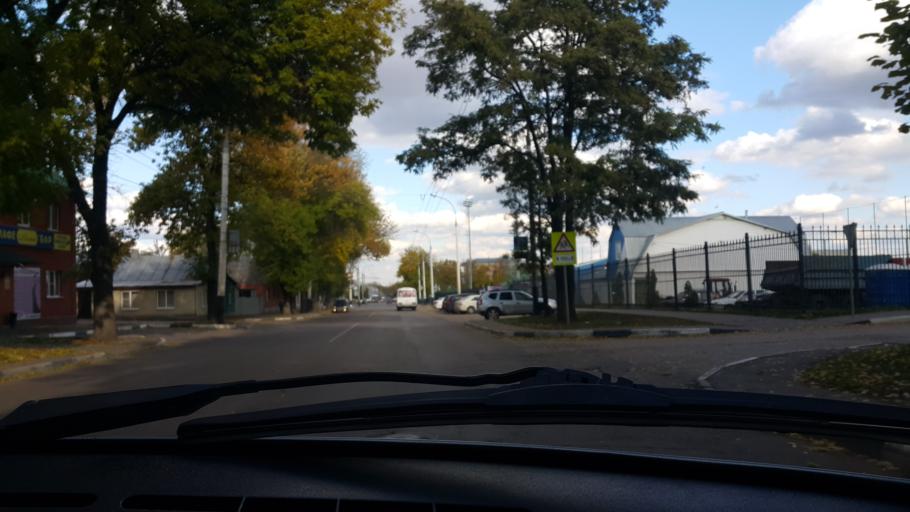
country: RU
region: Tambov
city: Pokrovo-Prigorodnoye
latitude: 52.7144
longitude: 41.4054
